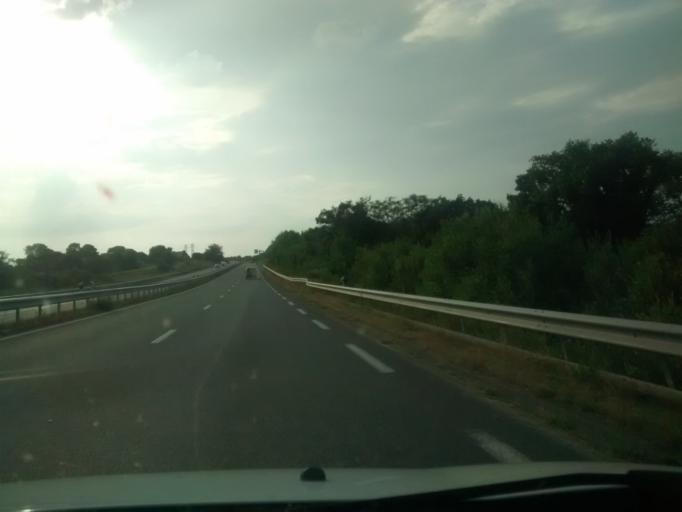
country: FR
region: Brittany
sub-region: Departement des Cotes-d'Armor
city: Rospez
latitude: 48.7121
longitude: -3.3898
